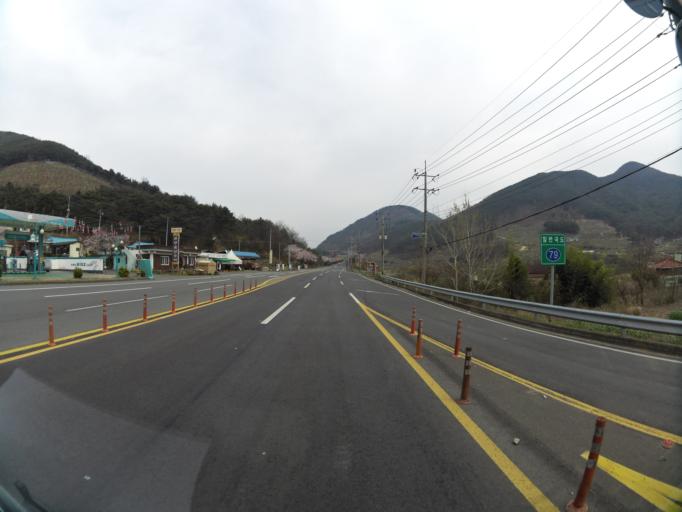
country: KR
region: Gyeongsangnam-do
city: Changnyeong
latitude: 35.4434
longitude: 128.5580
